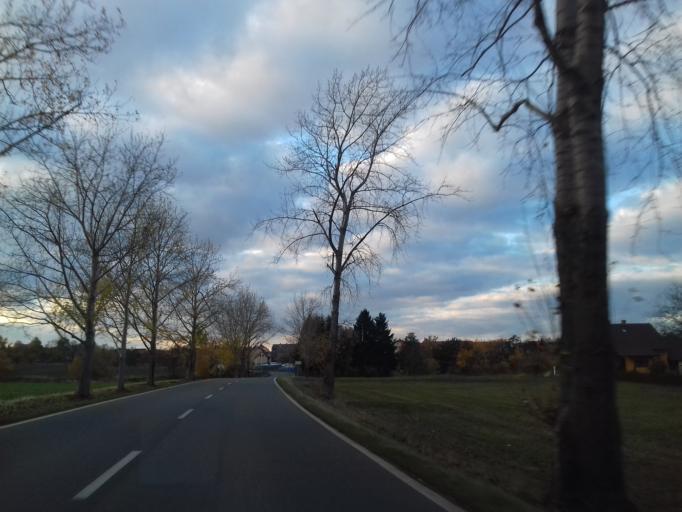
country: CZ
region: Pardubicky
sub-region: Okres Chrudim
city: Skutec
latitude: 49.8389
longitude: 16.0087
